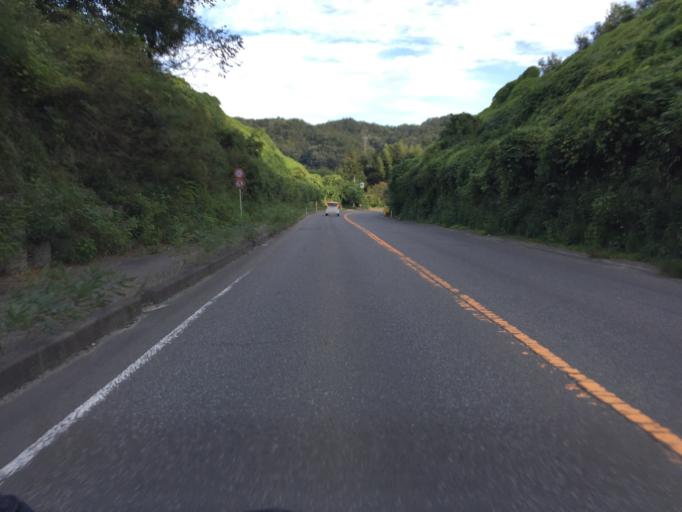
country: JP
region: Fukushima
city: Hobaramachi
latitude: 37.7754
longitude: 140.5939
